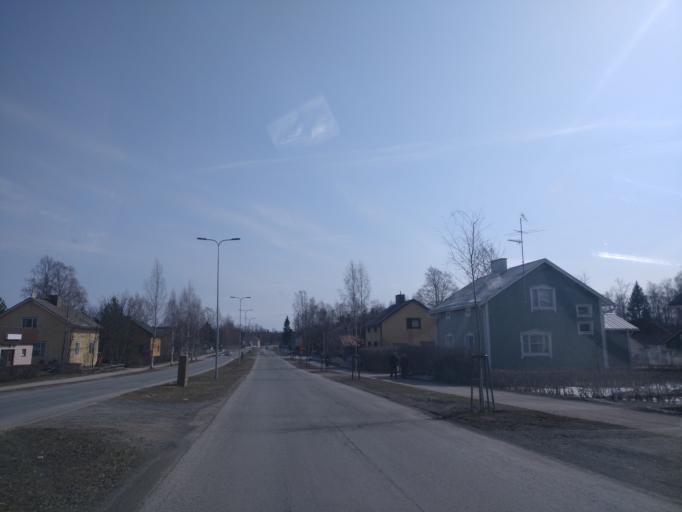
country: FI
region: Lapland
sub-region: Kemi-Tornio
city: Kemi
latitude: 65.7294
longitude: 24.6030
